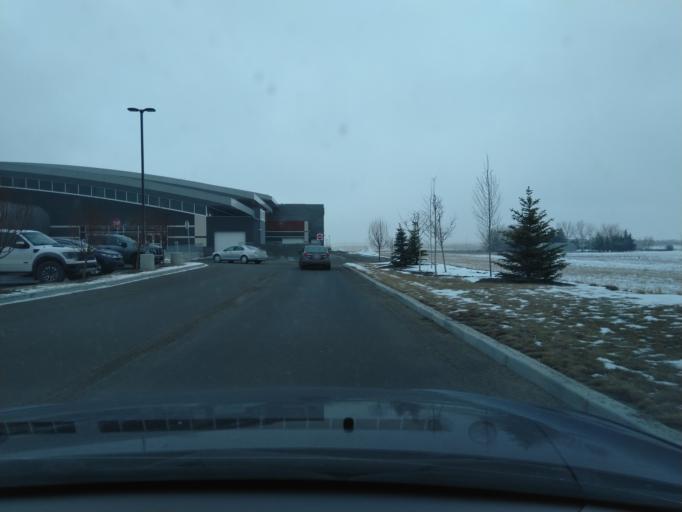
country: CA
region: Alberta
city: Airdrie
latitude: 51.1966
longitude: -113.9940
